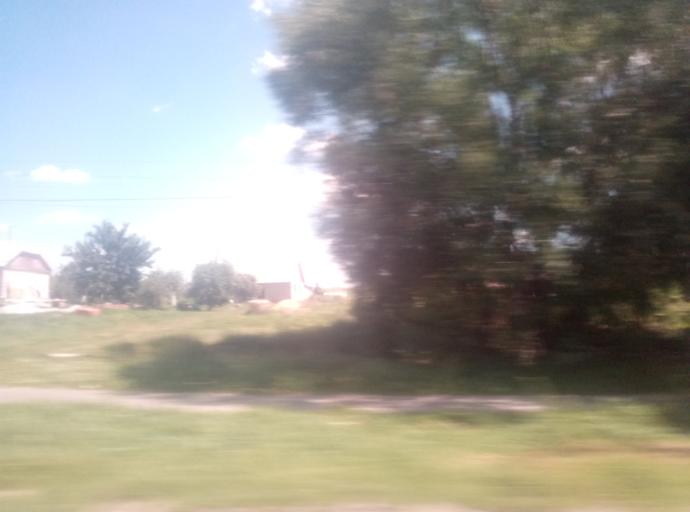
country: RU
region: Tula
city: Kireyevsk
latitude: 53.9852
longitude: 37.9327
